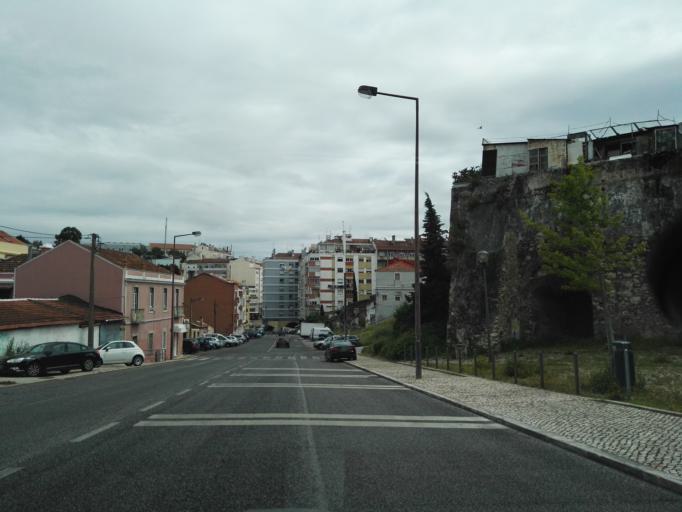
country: PT
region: Lisbon
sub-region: Oeiras
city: Alges
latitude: 38.7054
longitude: -9.1924
